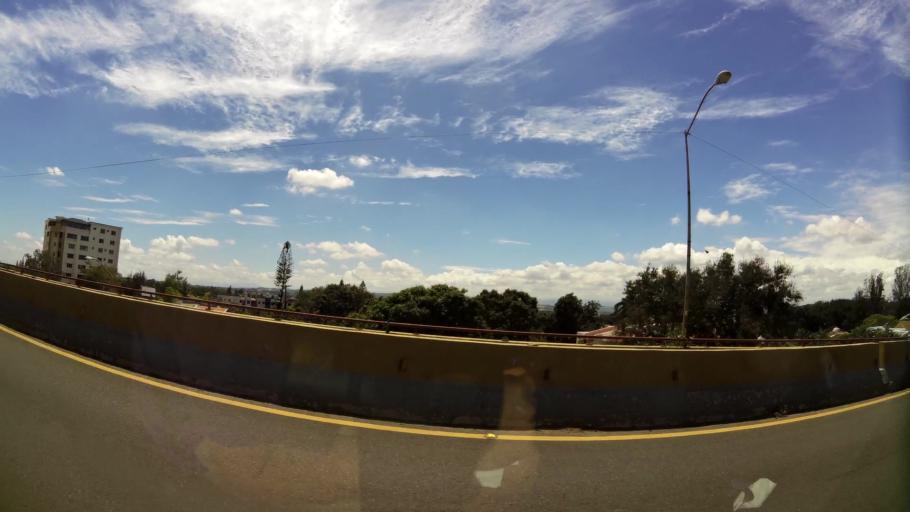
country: DO
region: Santiago
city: Santiago de los Caballeros
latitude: 19.4502
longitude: -70.6881
